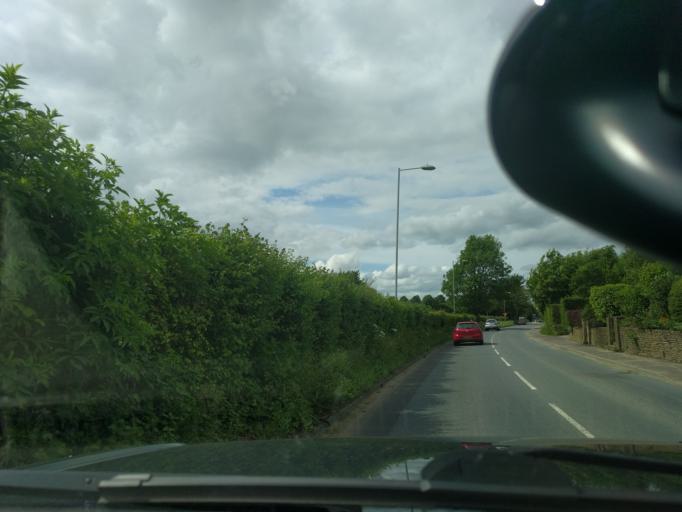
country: GB
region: England
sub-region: Wiltshire
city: Melksham
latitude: 51.3812
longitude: -2.1508
